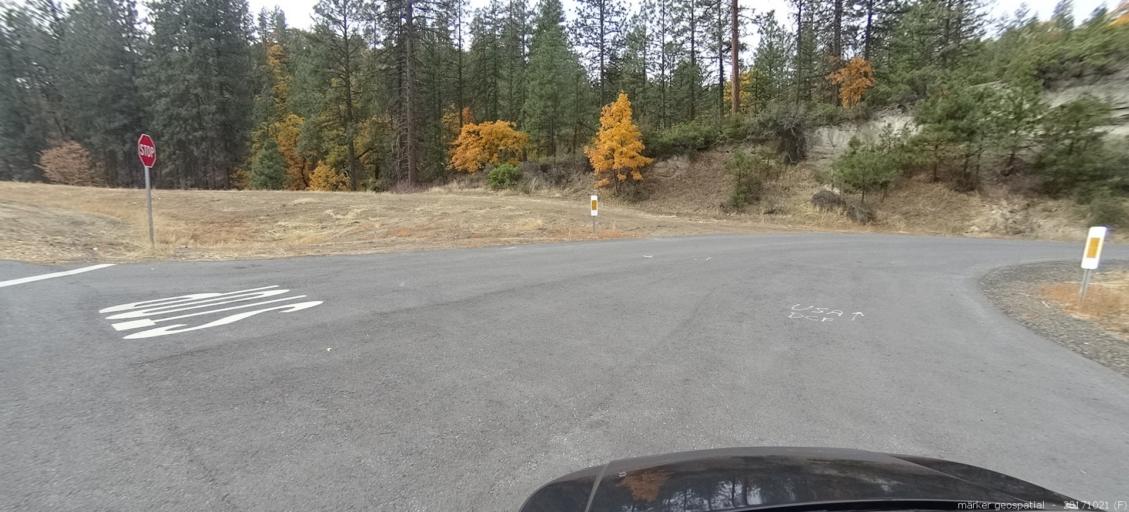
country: US
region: California
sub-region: Shasta County
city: Burney
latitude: 40.9748
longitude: -121.5632
